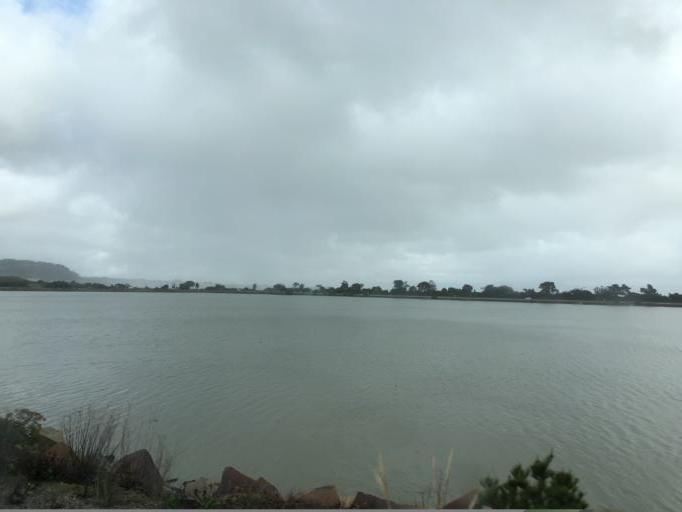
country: US
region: California
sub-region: San Mateo County
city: Brisbane
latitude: 37.6813
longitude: -122.3938
